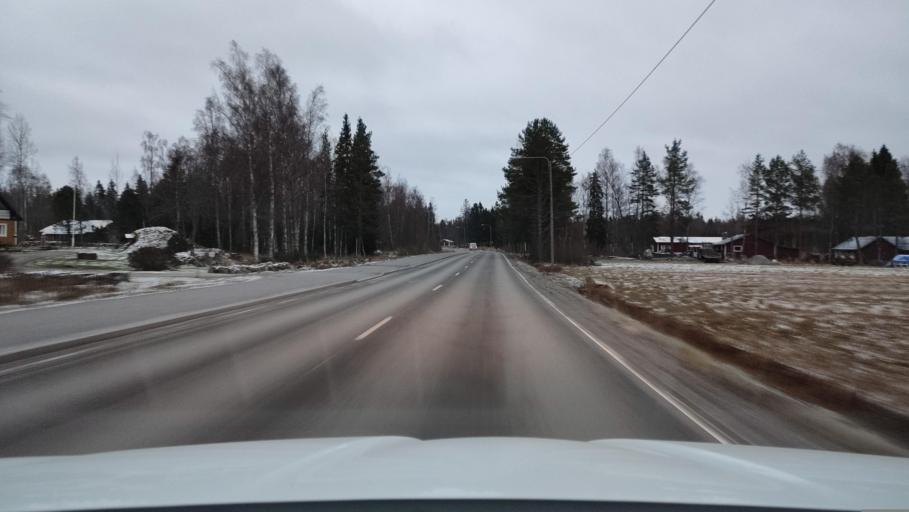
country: FI
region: Ostrobothnia
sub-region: Vaasa
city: Replot
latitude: 63.2224
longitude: 21.4129
